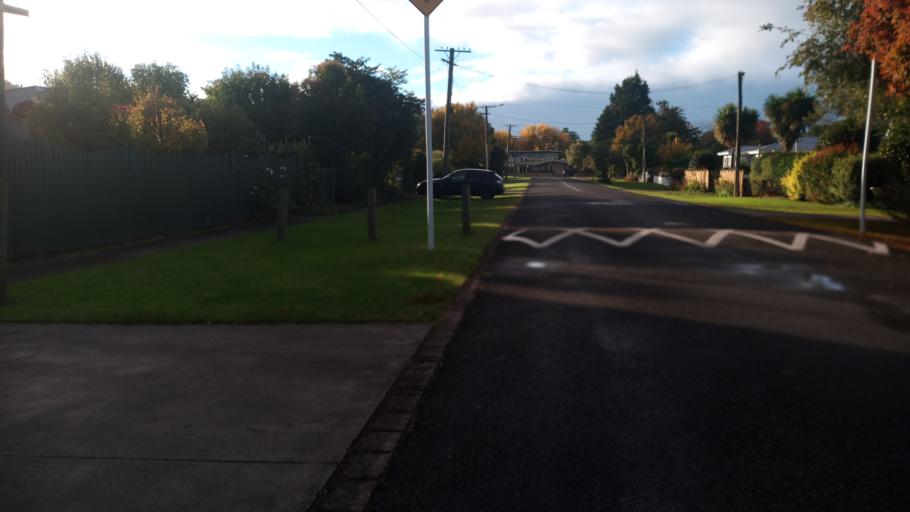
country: NZ
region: Gisborne
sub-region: Gisborne District
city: Gisborne
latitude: -38.6522
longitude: 178.0182
